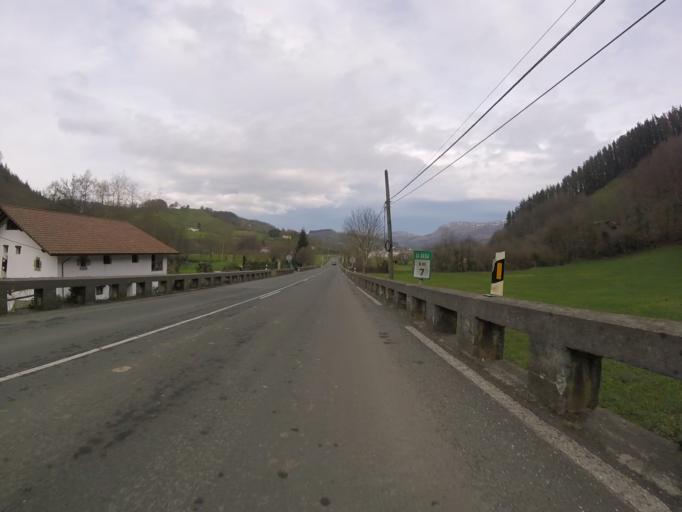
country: ES
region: Basque Country
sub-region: Provincia de Guipuzcoa
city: Albiztur
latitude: 43.1281
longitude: -2.1583
